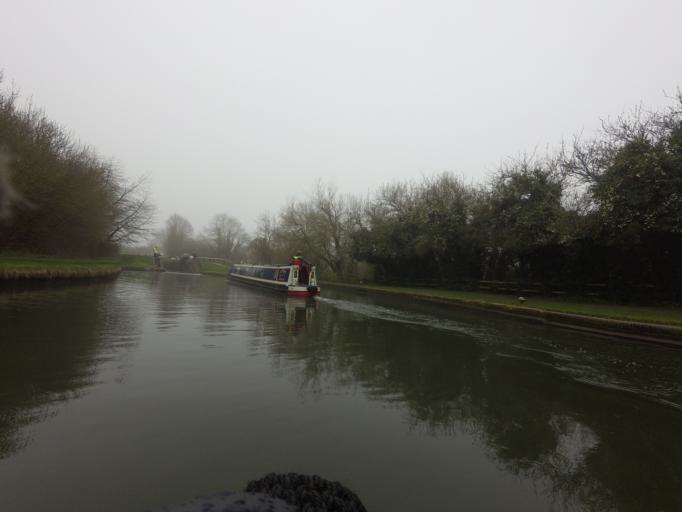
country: GB
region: England
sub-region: Hertfordshire
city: Tring
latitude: 51.8157
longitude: -0.6592
